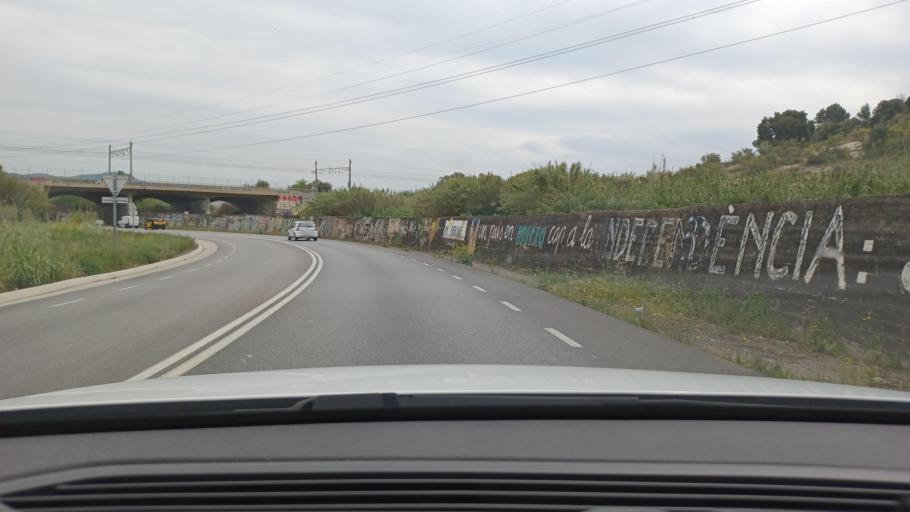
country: ES
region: Catalonia
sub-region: Provincia de Barcelona
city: Sant Vicenc dels Horts
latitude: 41.3851
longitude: 2.0127
